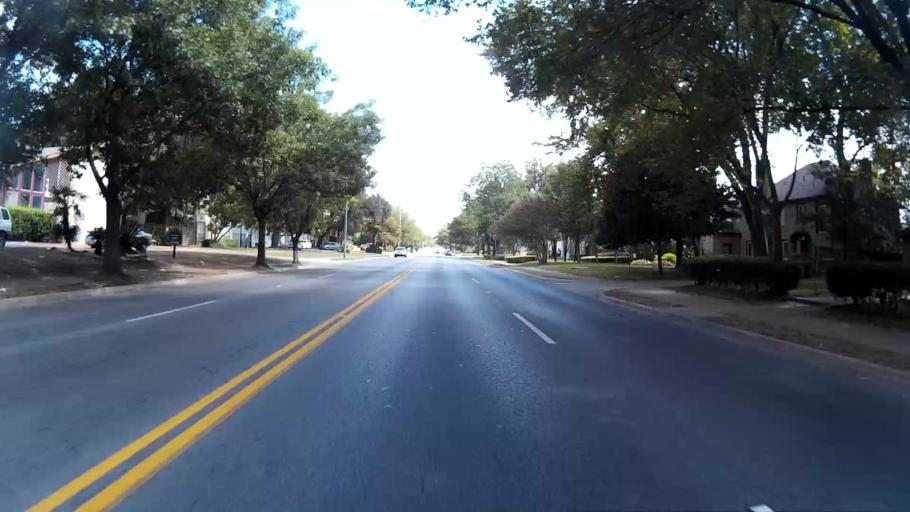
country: US
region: Texas
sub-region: Dallas County
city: Highland Park
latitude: 32.8042
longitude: -96.7644
